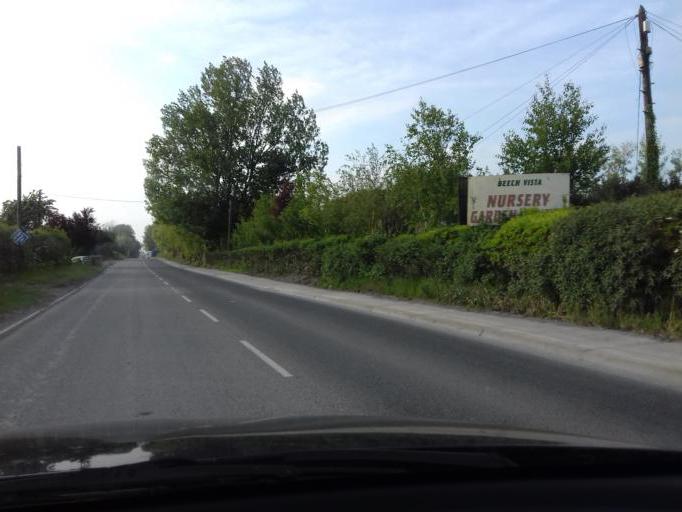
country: IE
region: Leinster
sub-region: Dublin City
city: Finglas
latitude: 53.4104
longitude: -6.3169
